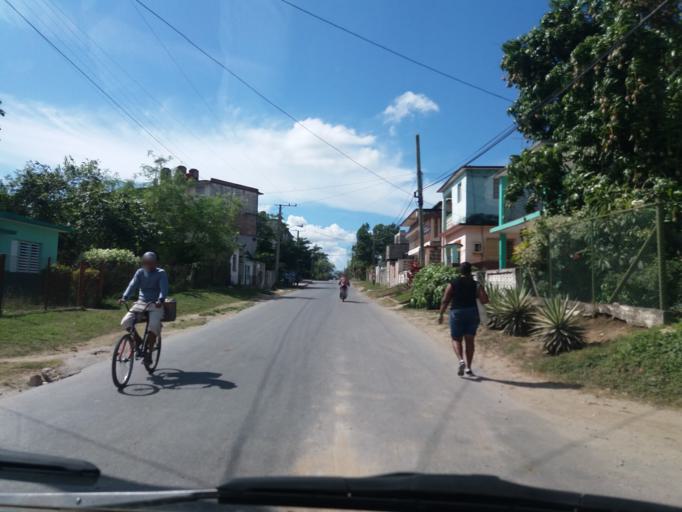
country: CU
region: Cienfuegos
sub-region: Municipio de Cienfuegos
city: Cienfuegos
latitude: 22.1508
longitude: -80.4278
